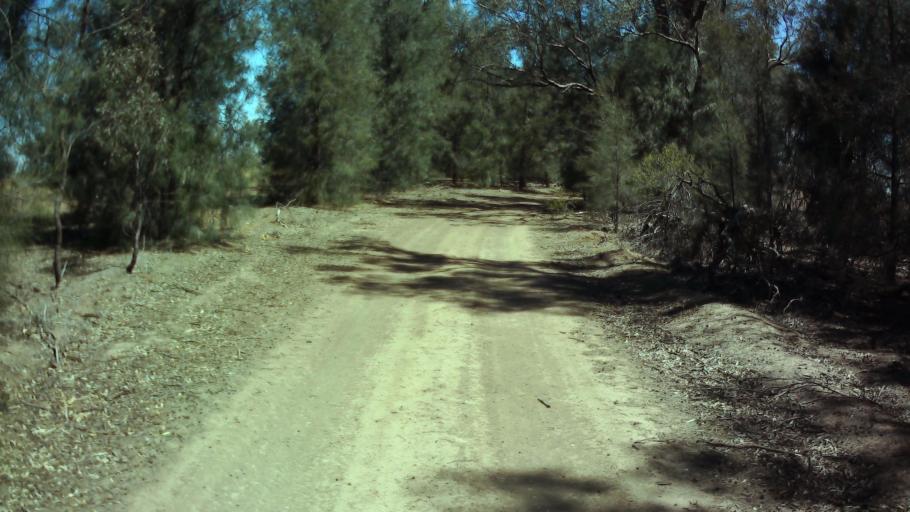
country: AU
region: New South Wales
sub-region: Bland
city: West Wyalong
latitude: -33.9221
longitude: 147.6825
